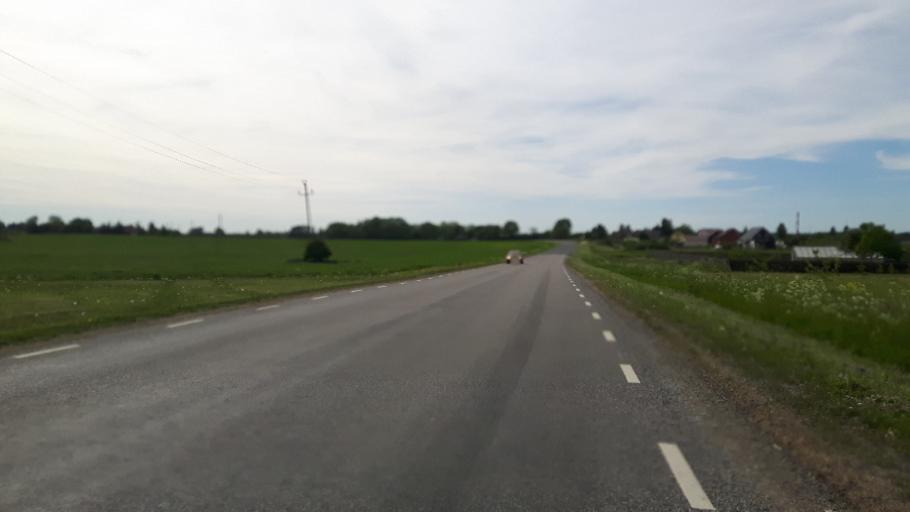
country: EE
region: Harju
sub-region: Joelaehtme vald
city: Loo
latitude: 59.4241
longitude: 25.0003
